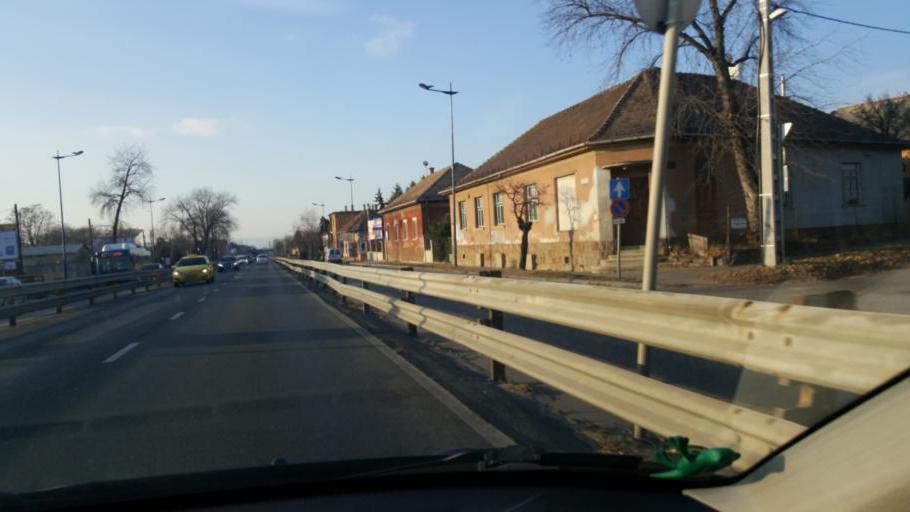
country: HU
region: Budapest
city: Budapest XVIII. keruelet
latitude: 47.4542
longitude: 19.1912
